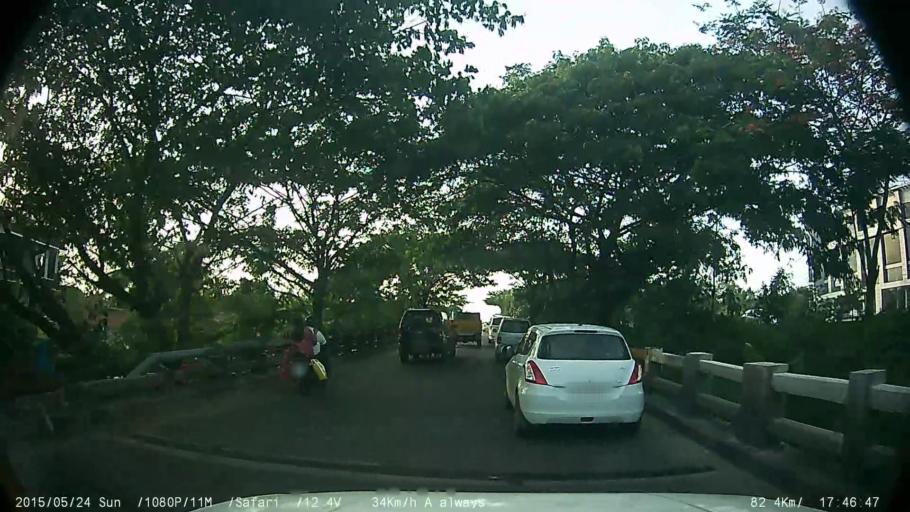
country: IN
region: Kerala
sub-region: Ernakulam
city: Cochin
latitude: 9.9720
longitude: 76.3179
